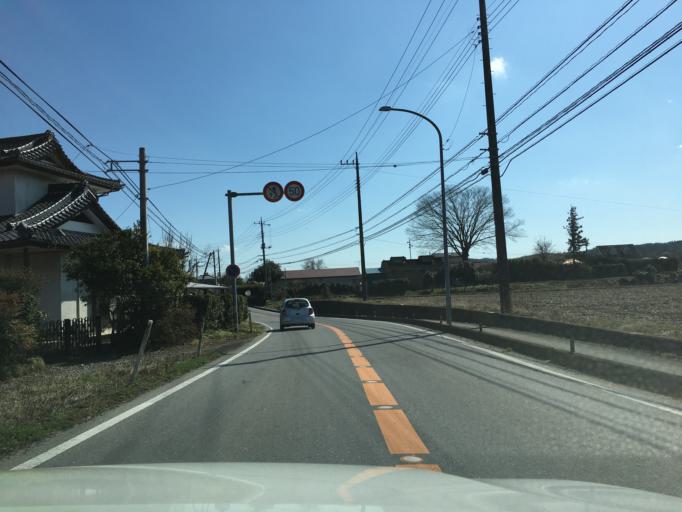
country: JP
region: Tochigi
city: Karasuyama
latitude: 36.7368
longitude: 140.1379
